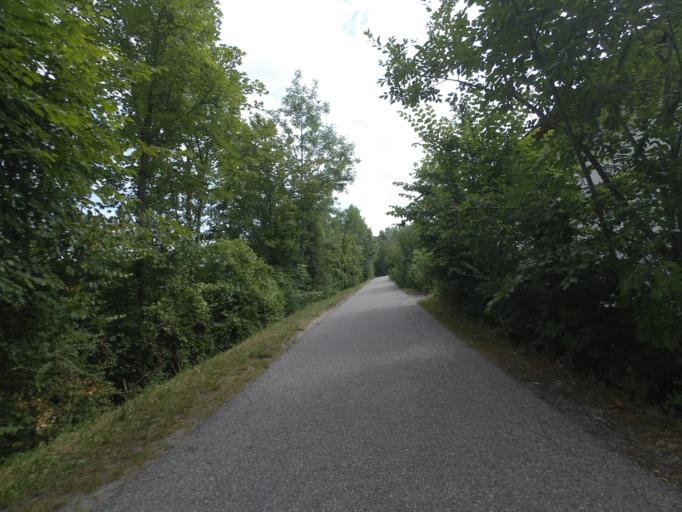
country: DE
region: Bavaria
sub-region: Upper Bavaria
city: Ainring
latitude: 47.7920
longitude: 12.9534
